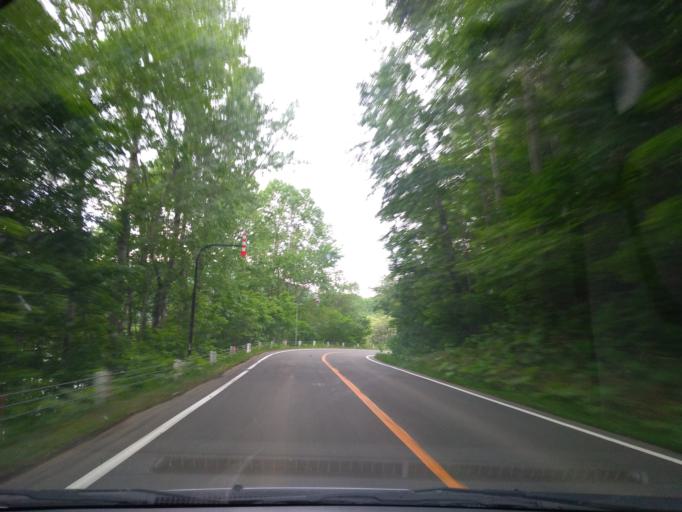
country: JP
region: Hokkaido
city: Shimo-furano
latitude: 43.1382
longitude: 142.4618
